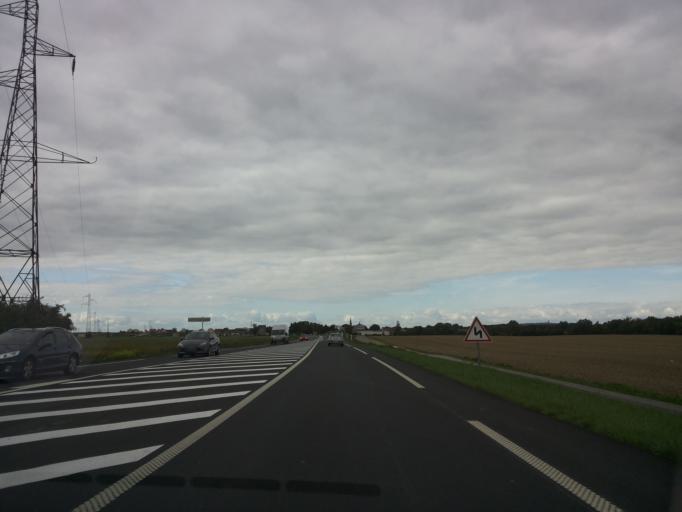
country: FR
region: Champagne-Ardenne
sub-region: Departement de la Marne
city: Verzy
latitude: 49.1655
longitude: 4.1954
